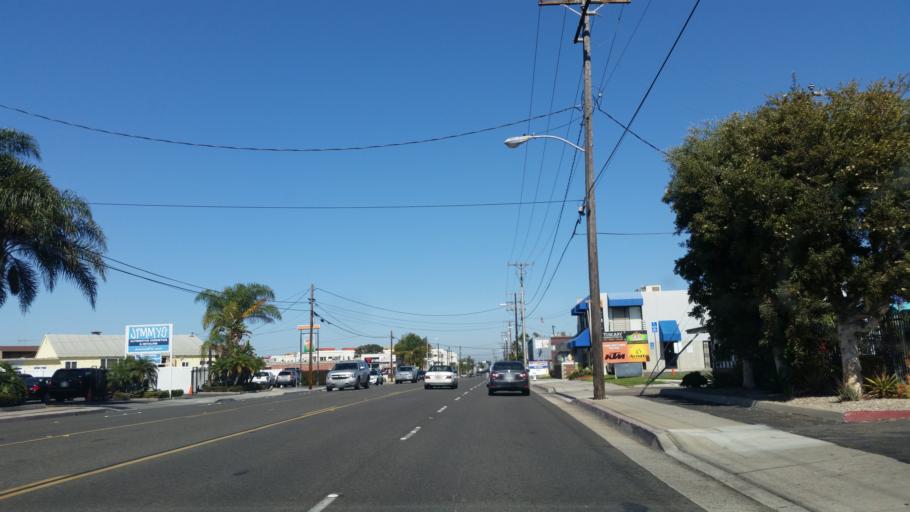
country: US
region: California
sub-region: Orange County
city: Costa Mesa
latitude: 33.6329
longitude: -117.9267
